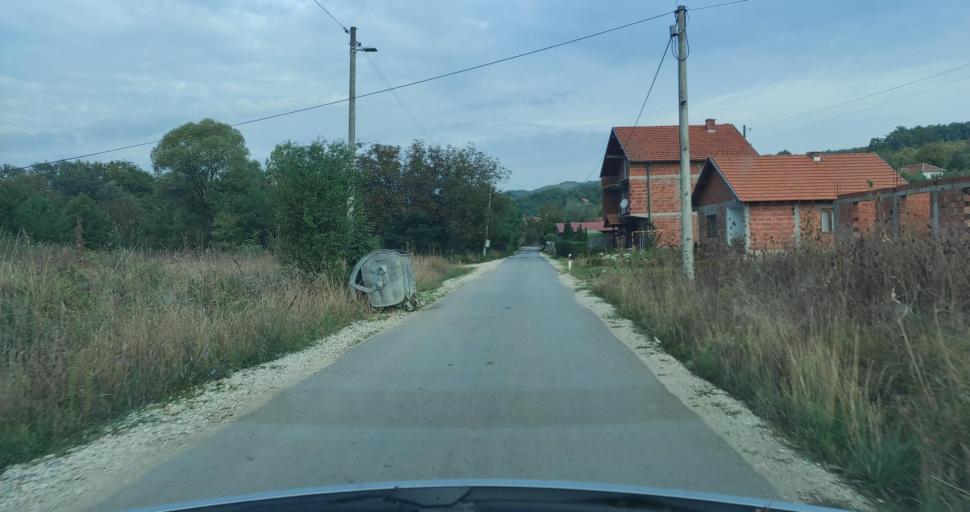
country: RS
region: Central Serbia
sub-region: Pcinjski Okrug
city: Vladicin Han
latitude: 42.6690
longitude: 22.0309
